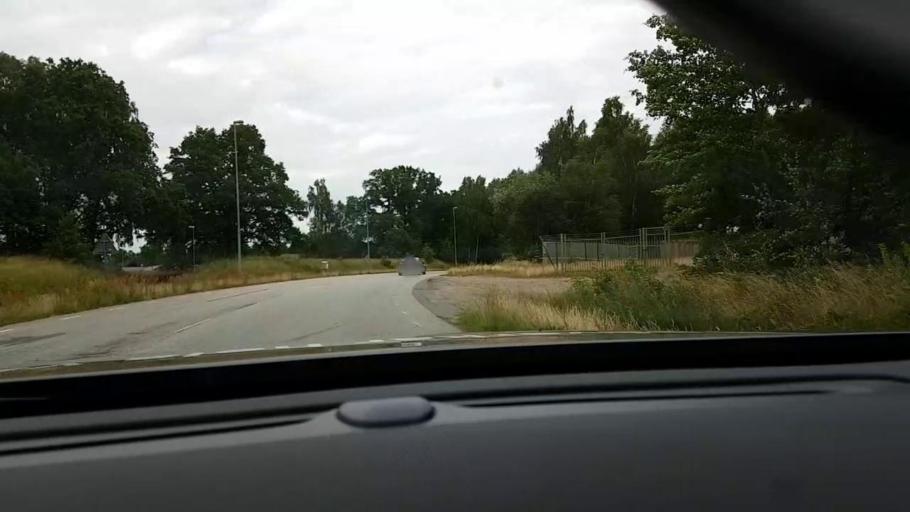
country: SE
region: Skane
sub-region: Hassleholms Kommun
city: Hassleholm
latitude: 56.1699
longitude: 13.8013
